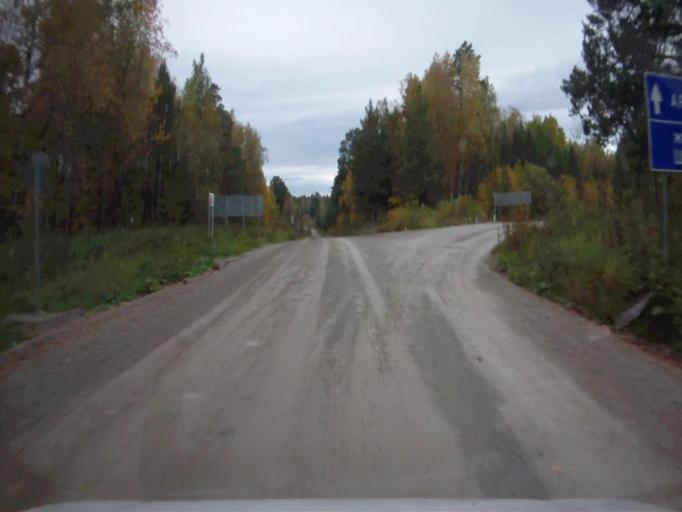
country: RU
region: Chelyabinsk
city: Nyazepetrovsk
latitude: 56.0865
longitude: 59.4183
